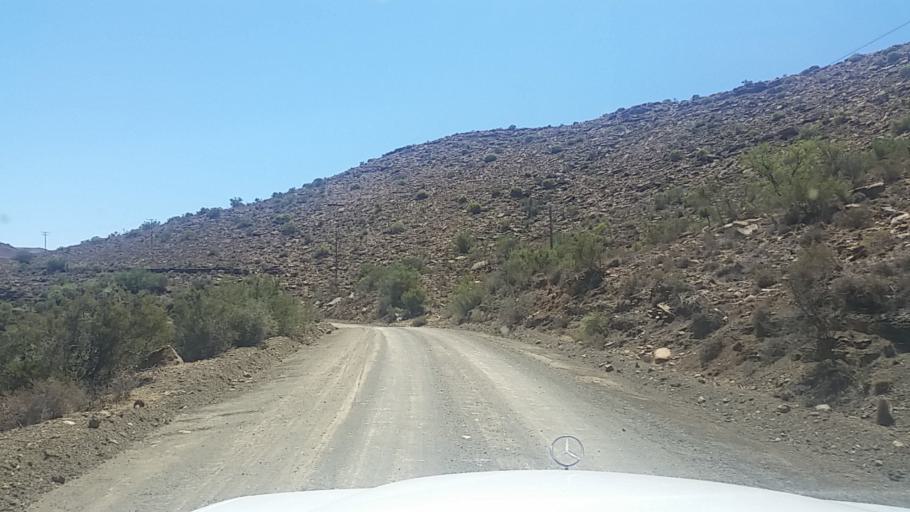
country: ZA
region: Eastern Cape
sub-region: Cacadu District Municipality
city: Graaff-Reinet
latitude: -31.8571
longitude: 24.5530
